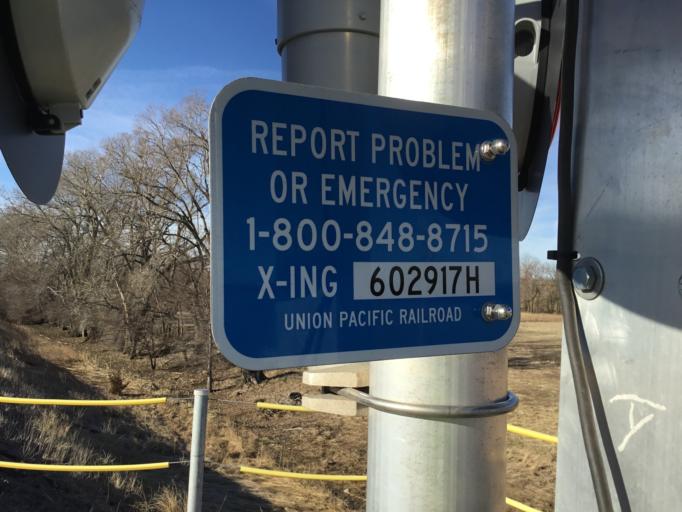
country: US
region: Kansas
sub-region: Marion County
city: Hillsboro
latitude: 38.4165
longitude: -97.3902
